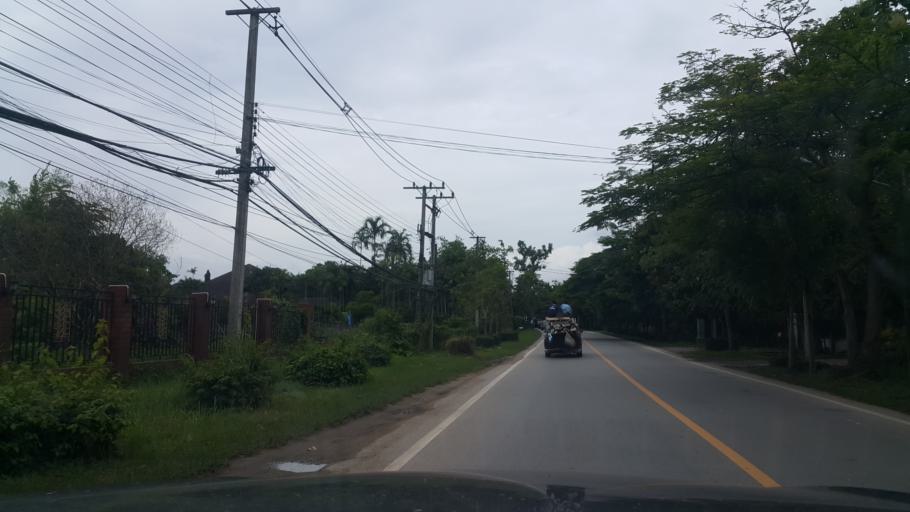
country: TH
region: Chiang Mai
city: San Sai
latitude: 18.8640
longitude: 99.0523
